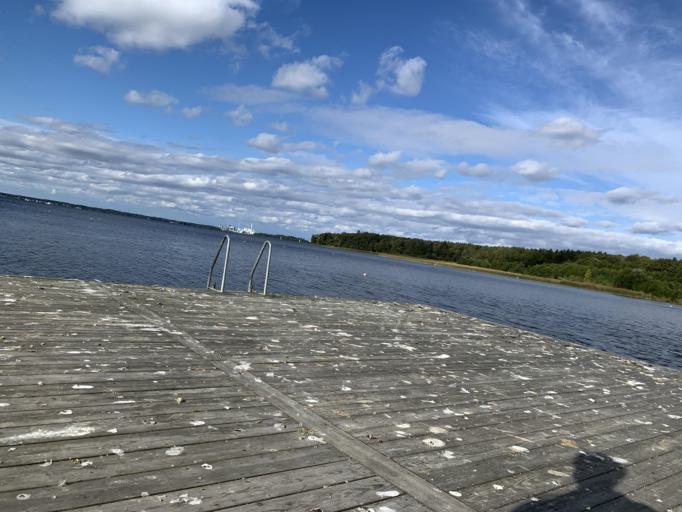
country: SE
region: Vaestmanland
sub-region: Vasteras
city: Vasteras
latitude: 59.5651
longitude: 16.6192
